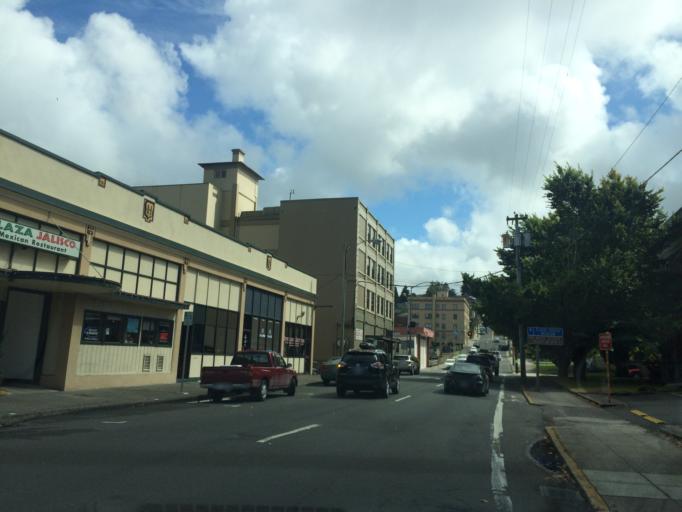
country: US
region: Oregon
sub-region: Clatsop County
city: Astoria
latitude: 46.1898
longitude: -123.8348
